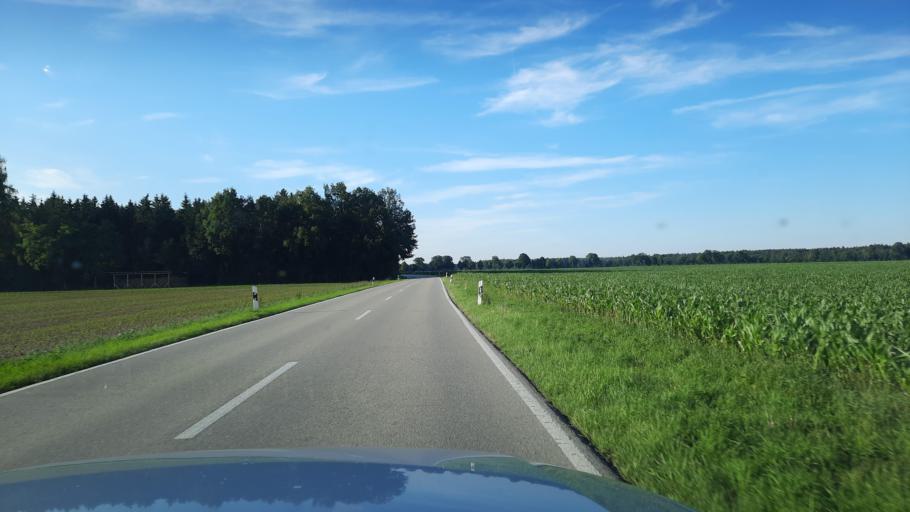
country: DE
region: Bavaria
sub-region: Upper Bavaria
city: Grasbrunn
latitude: 48.0657
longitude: 11.7735
